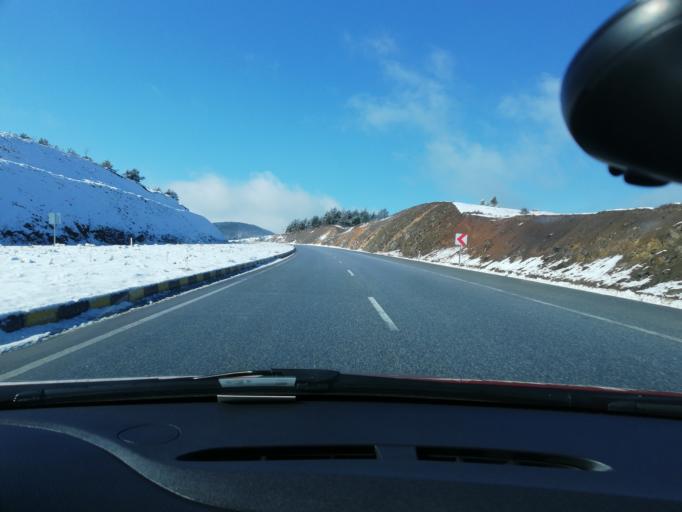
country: TR
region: Kastamonu
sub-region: Cide
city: Kastamonu
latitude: 41.3543
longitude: 33.6610
